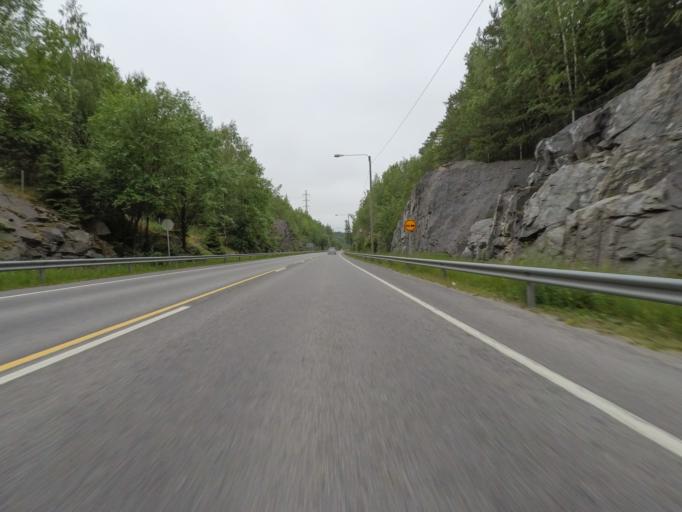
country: FI
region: Varsinais-Suomi
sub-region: Turku
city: Raisio
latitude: 60.4626
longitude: 22.1449
